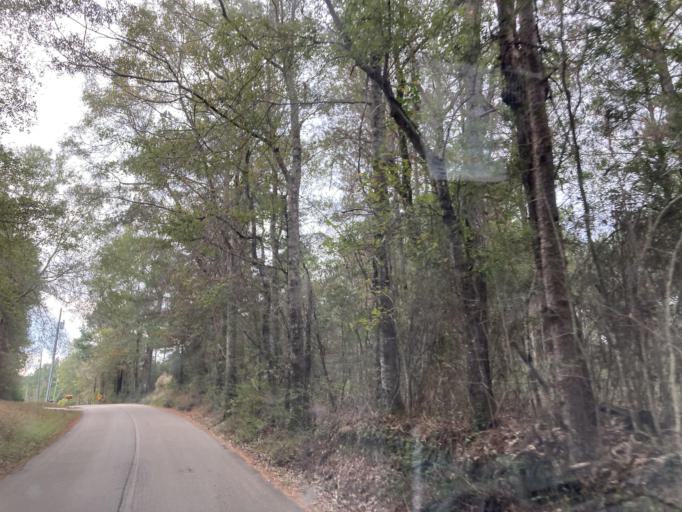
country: US
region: Mississippi
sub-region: Lamar County
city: Purvis
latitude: 31.1464
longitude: -89.4612
